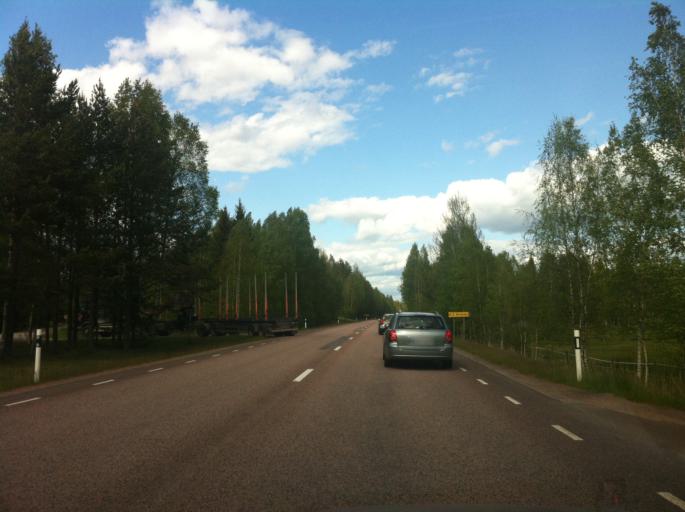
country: SE
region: Vaermland
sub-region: Kristinehamns Kommun
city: Kristinehamn
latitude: 59.3362
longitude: 14.1227
